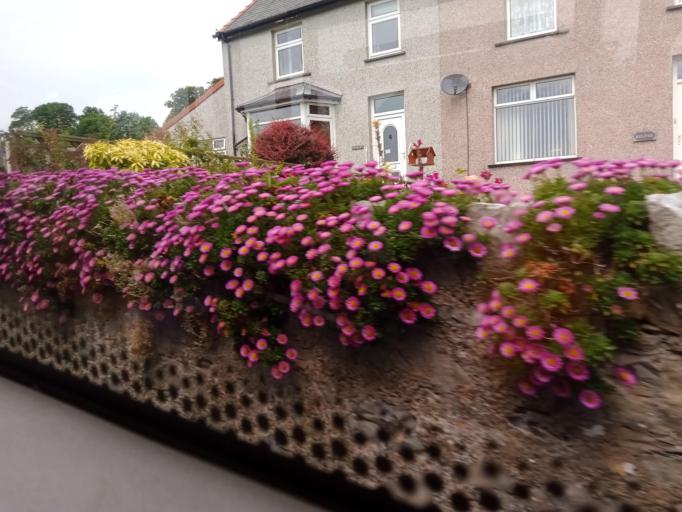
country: GB
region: Wales
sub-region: Anglesey
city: Llangoed
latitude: 53.2977
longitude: -4.0706
